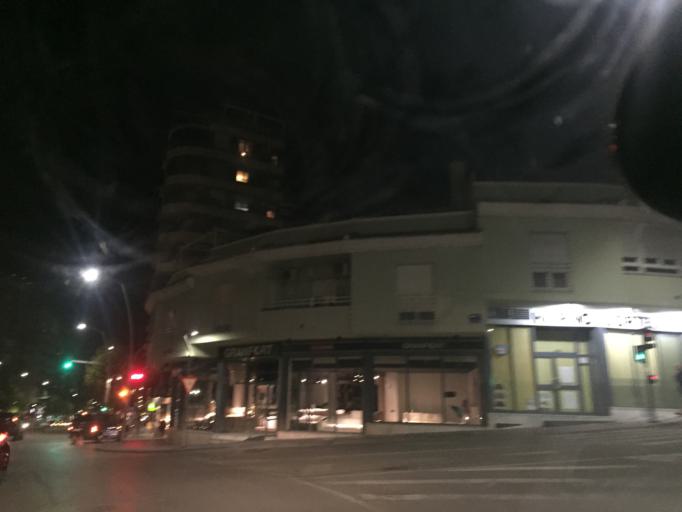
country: ES
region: Andalusia
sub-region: Provincia de Jaen
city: Jaen
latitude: 37.7780
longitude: -3.8020
